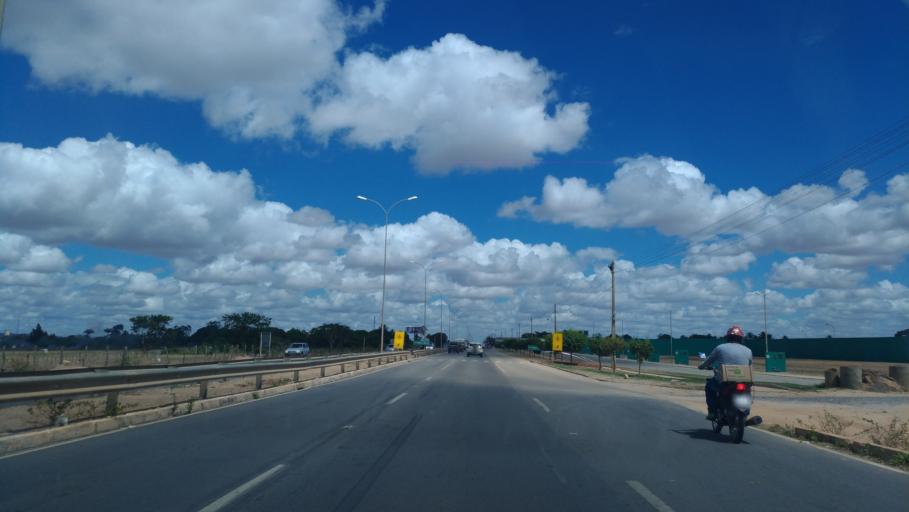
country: BR
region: Alagoas
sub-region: Arapiraca
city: Arapiraca
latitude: -9.7304
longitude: -36.6607
